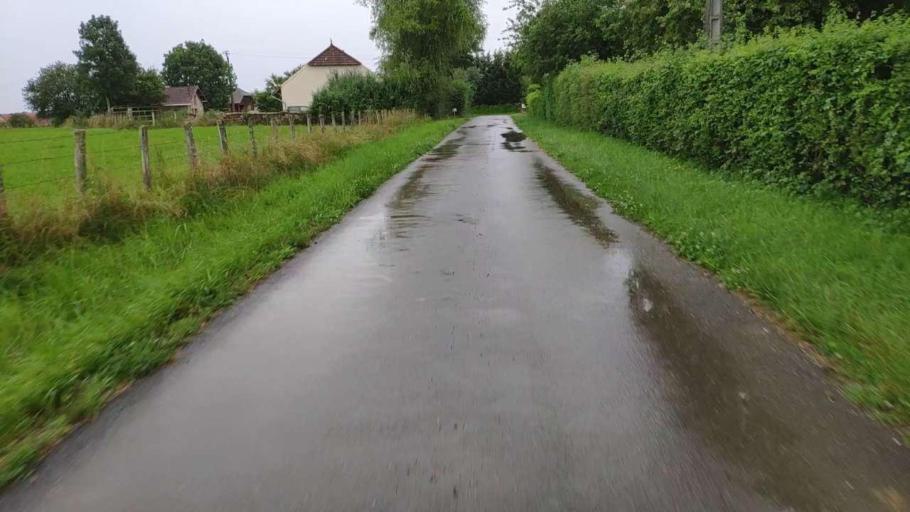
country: FR
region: Franche-Comte
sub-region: Departement du Jura
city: Chaussin
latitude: 46.8780
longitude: 5.4144
